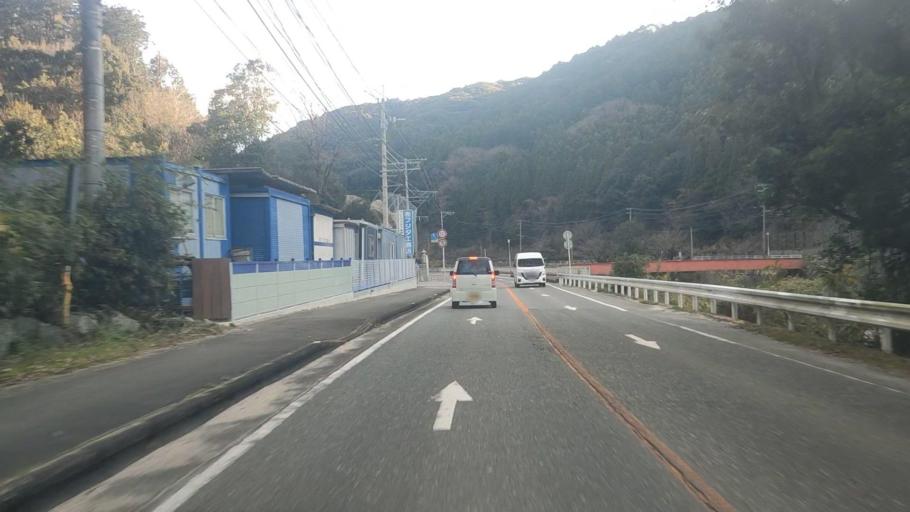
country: JP
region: Saga Prefecture
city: Saga-shi
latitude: 33.3339
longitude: 130.2627
